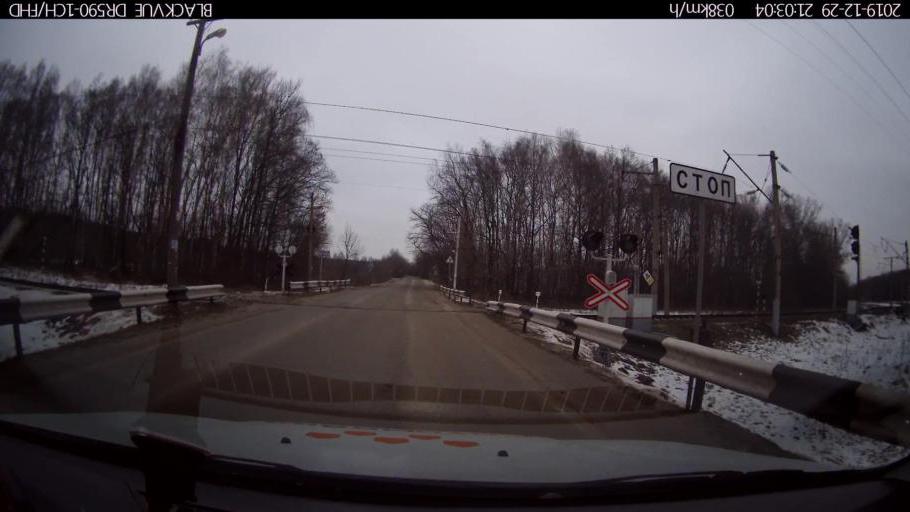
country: RU
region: Nizjnij Novgorod
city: Afonino
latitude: 56.1941
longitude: 44.0051
